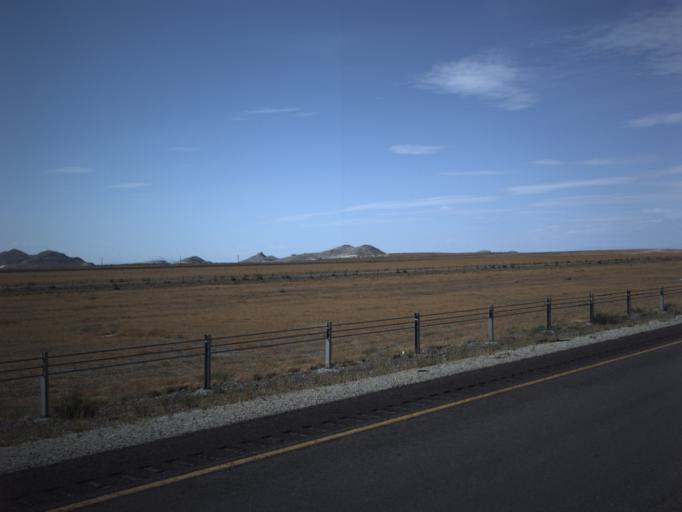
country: US
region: Utah
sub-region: Tooele County
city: Grantsville
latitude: 40.7272
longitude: -113.2457
